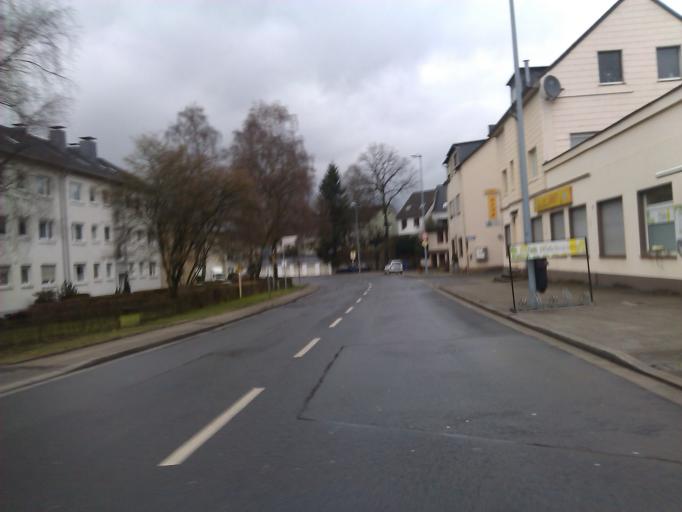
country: DE
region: North Rhine-Westphalia
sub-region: Regierungsbezirk Dusseldorf
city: Heiligenhaus
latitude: 51.3533
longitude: 6.9314
